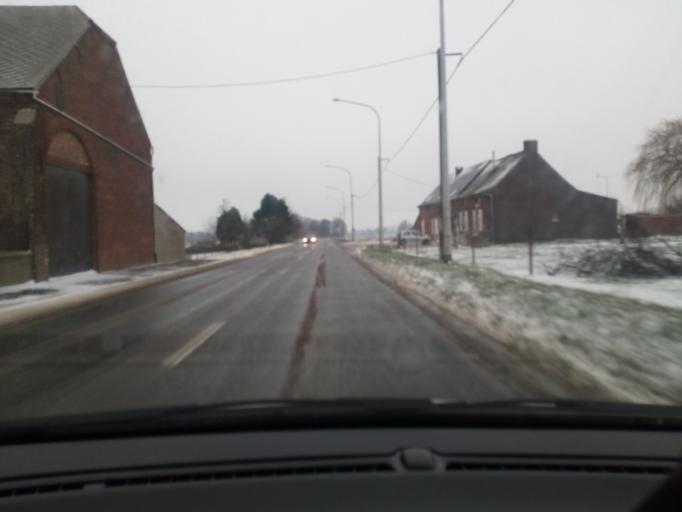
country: FR
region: Nord-Pas-de-Calais
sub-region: Departement du Nord
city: La Longueville
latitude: 50.3409
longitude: 3.8763
